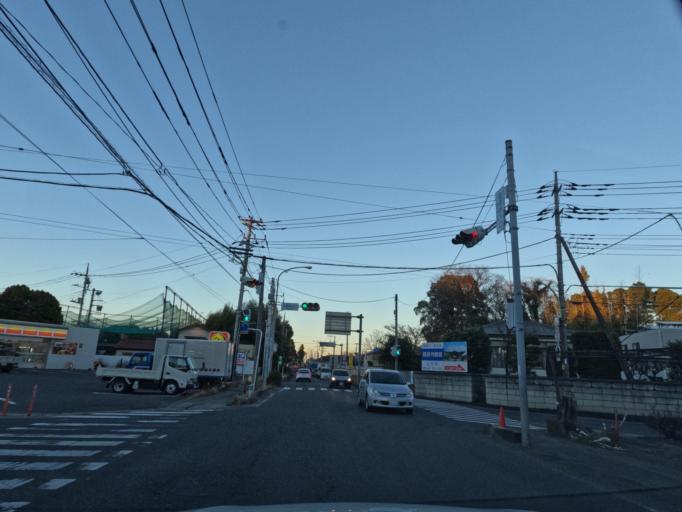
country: JP
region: Saitama
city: Iwatsuki
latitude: 35.9829
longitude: 139.6990
